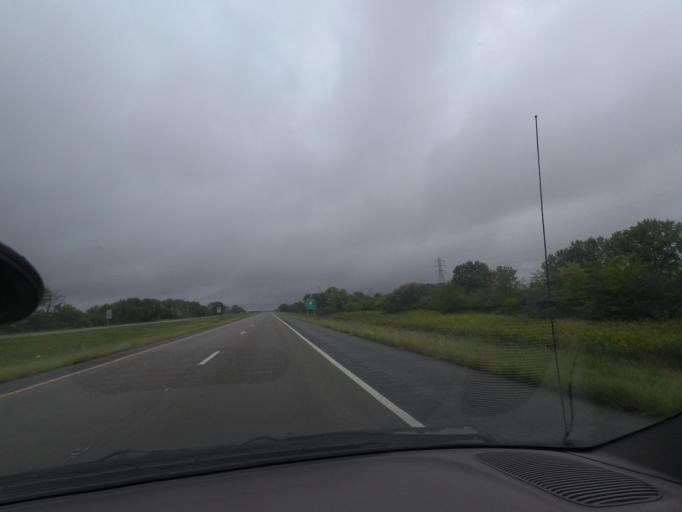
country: US
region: Illinois
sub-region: Piatt County
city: Monticello
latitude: 40.0972
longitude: -88.4974
